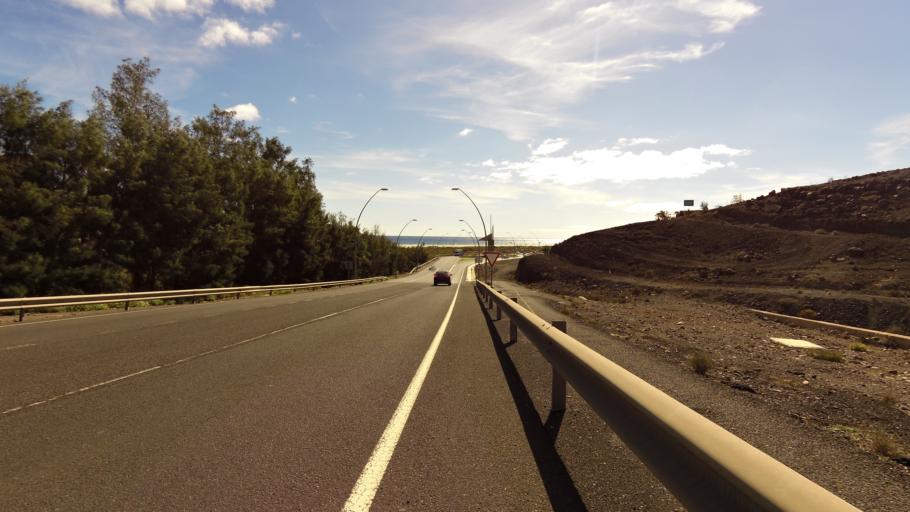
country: ES
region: Canary Islands
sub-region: Provincia de Las Palmas
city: Pajara
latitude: 28.0563
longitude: -14.3219
